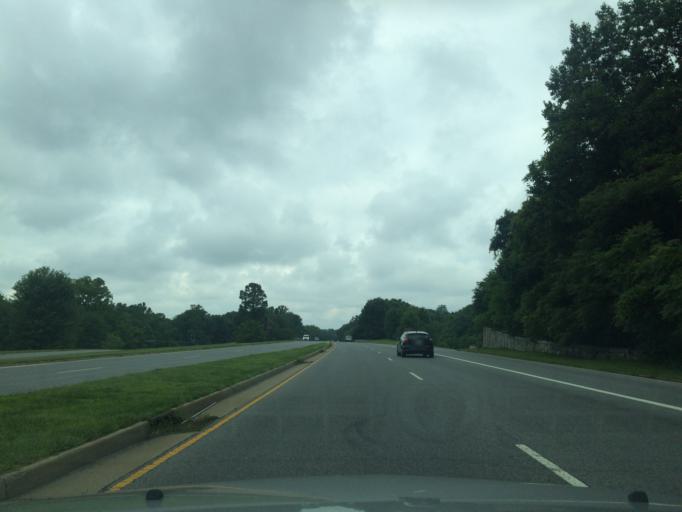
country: US
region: Maryland
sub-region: Prince George's County
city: Morningside
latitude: 38.8361
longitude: -76.8997
